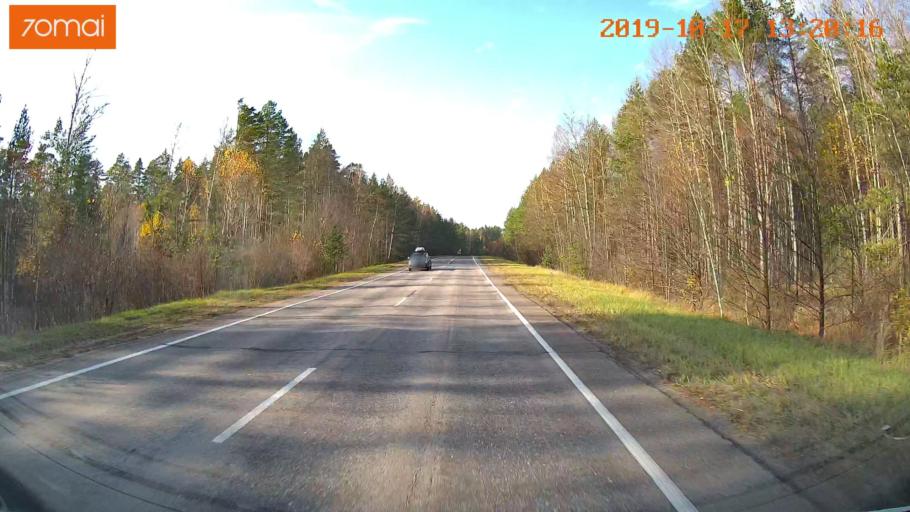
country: RU
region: Rjazan
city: Gus'-Zheleznyy
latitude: 55.0747
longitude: 41.0543
